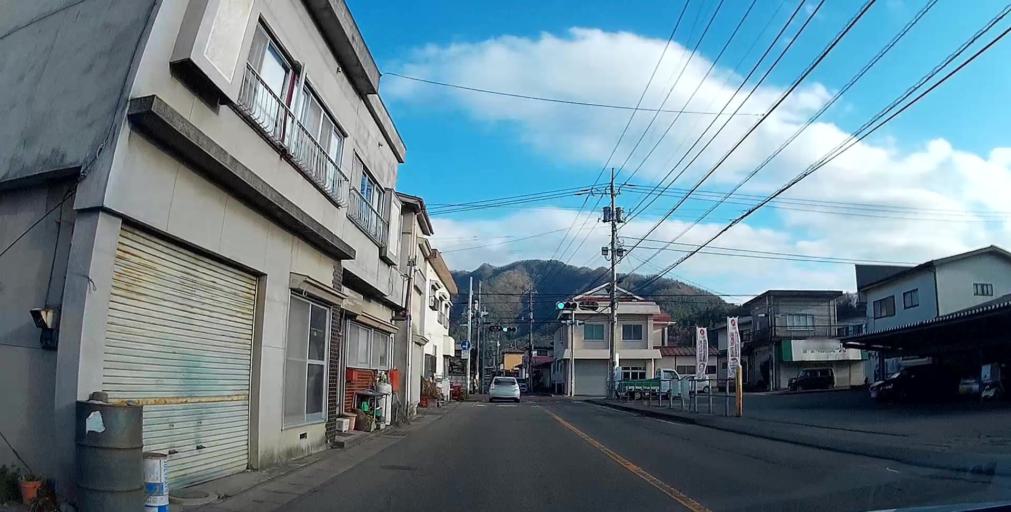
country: JP
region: Yamanashi
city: Fujikawaguchiko
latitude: 35.4943
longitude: 138.8240
